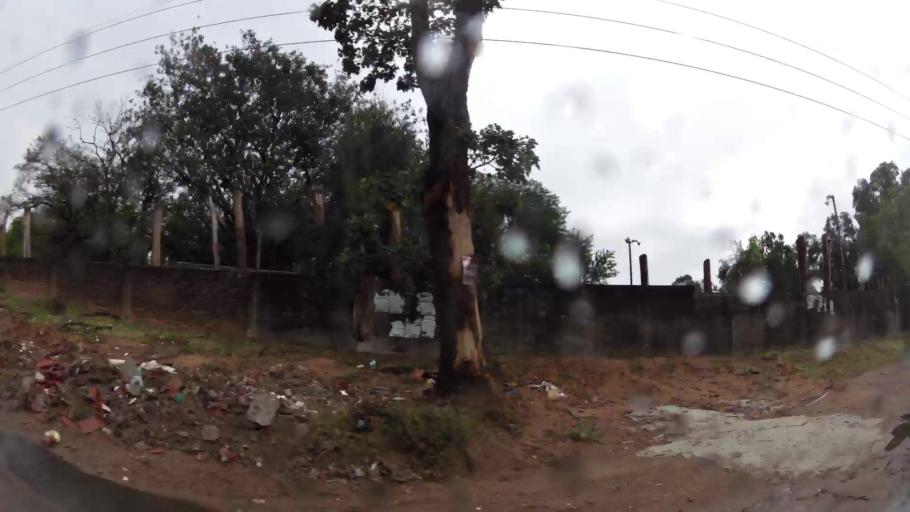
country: BO
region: Santa Cruz
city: Santa Cruz de la Sierra
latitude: -17.8029
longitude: -63.1596
